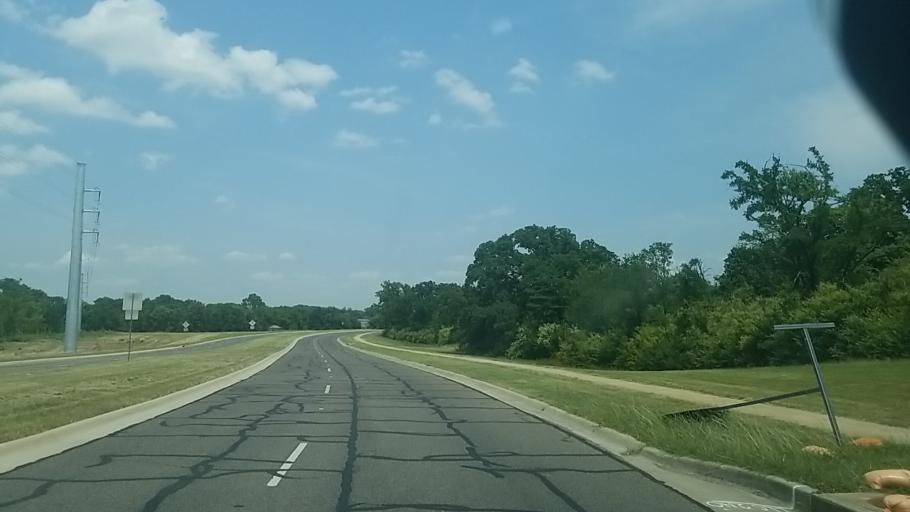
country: US
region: Texas
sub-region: Denton County
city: Denton
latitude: 33.2038
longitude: -97.0947
